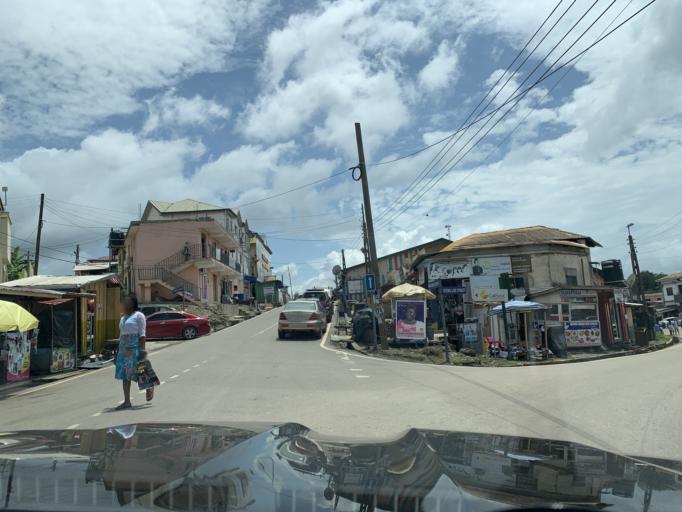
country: GH
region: Western
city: Tarkwa
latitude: 5.3046
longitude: -1.9916
